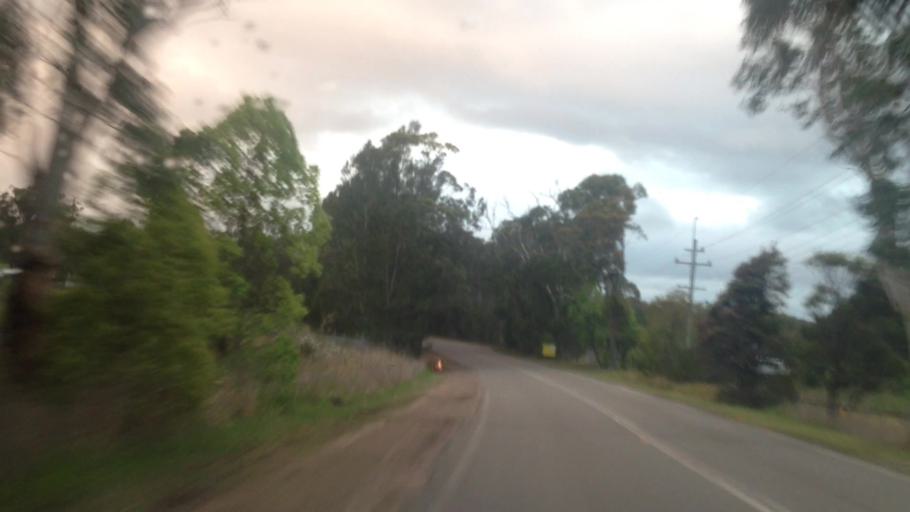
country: AU
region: New South Wales
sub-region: Lake Macquarie Shire
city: Dora Creek
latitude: -33.1065
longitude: 151.4767
